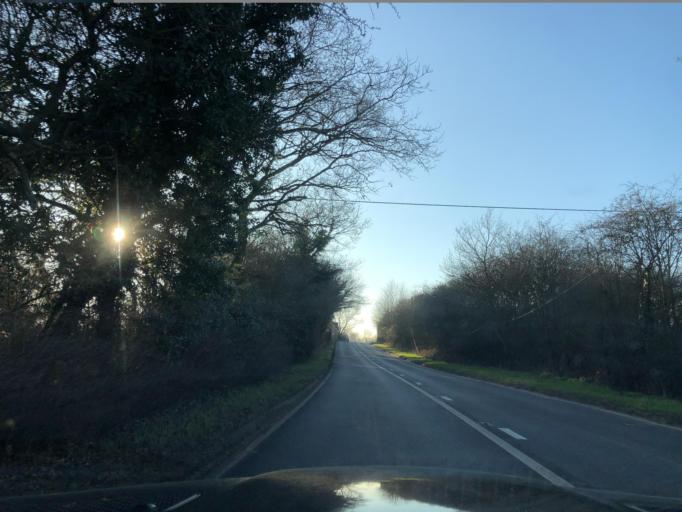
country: GB
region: England
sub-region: Warwickshire
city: Warwick
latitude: 52.2737
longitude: -1.6456
